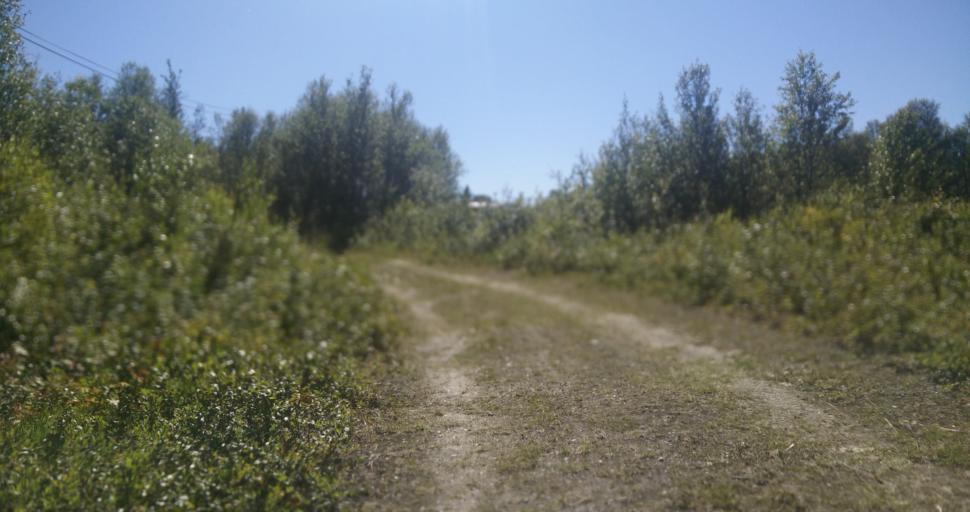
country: NO
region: Sor-Trondelag
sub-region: Tydal
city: Aas
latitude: 62.6446
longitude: 12.4282
